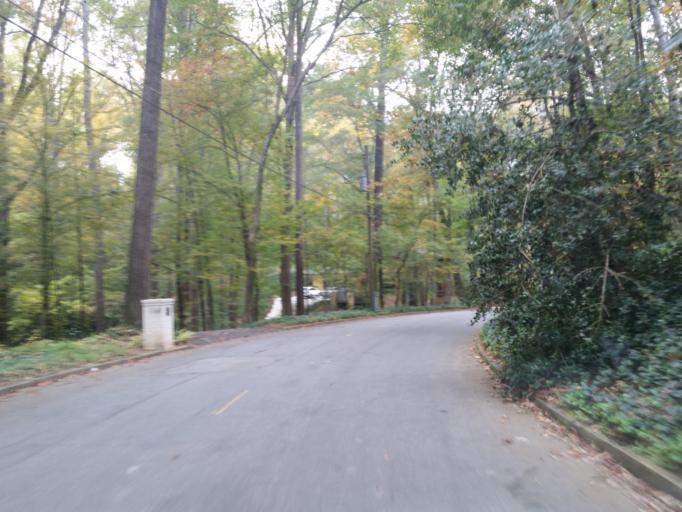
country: US
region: Georgia
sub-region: Cobb County
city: Vinings
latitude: 33.8537
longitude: -84.4252
